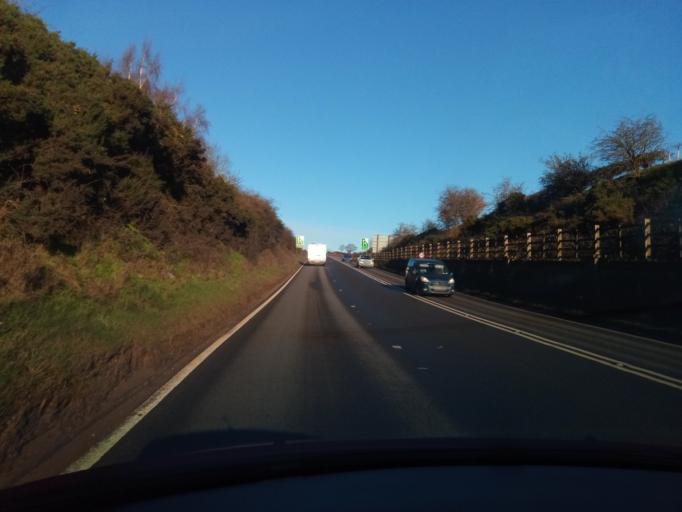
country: GB
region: England
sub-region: Nottinghamshire
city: Farnsfield
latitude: 53.1104
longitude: -1.0642
